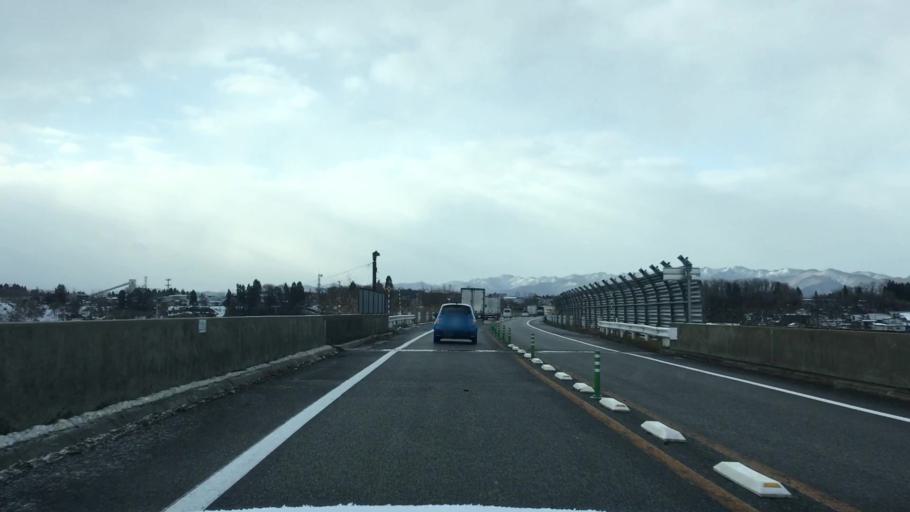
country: JP
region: Akita
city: Odate
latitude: 40.2823
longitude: 140.5399
